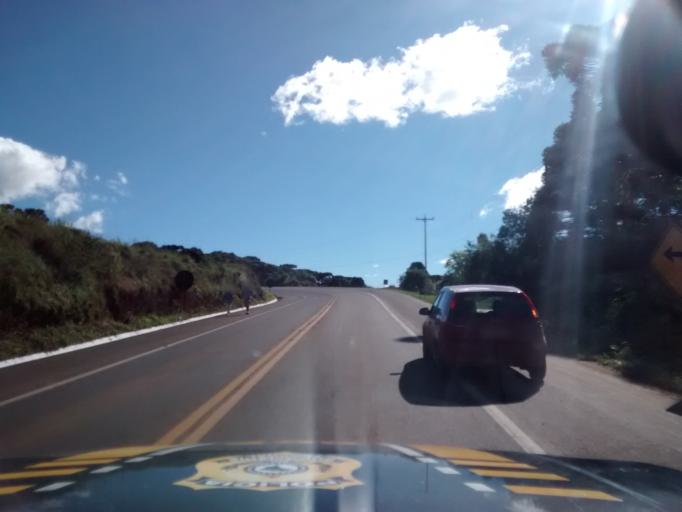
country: BR
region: Rio Grande do Sul
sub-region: Vacaria
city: Vacaria
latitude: -28.3241
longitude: -51.1915
